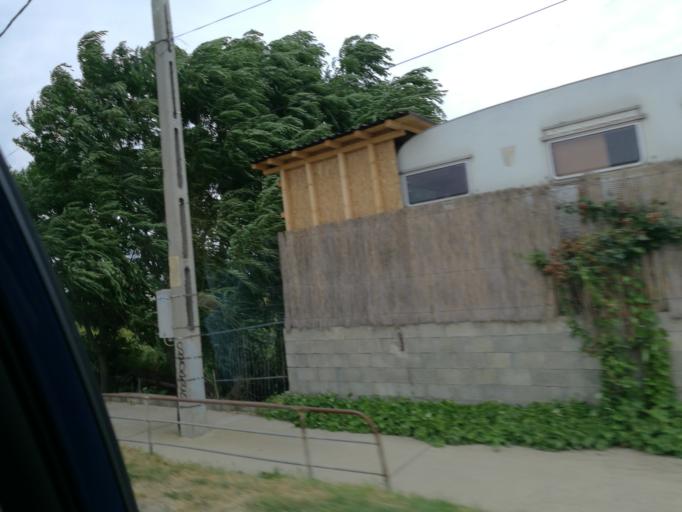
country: RO
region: Constanta
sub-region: Municipiul Mangalia
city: Mangalia
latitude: 43.7559
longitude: 28.5721
